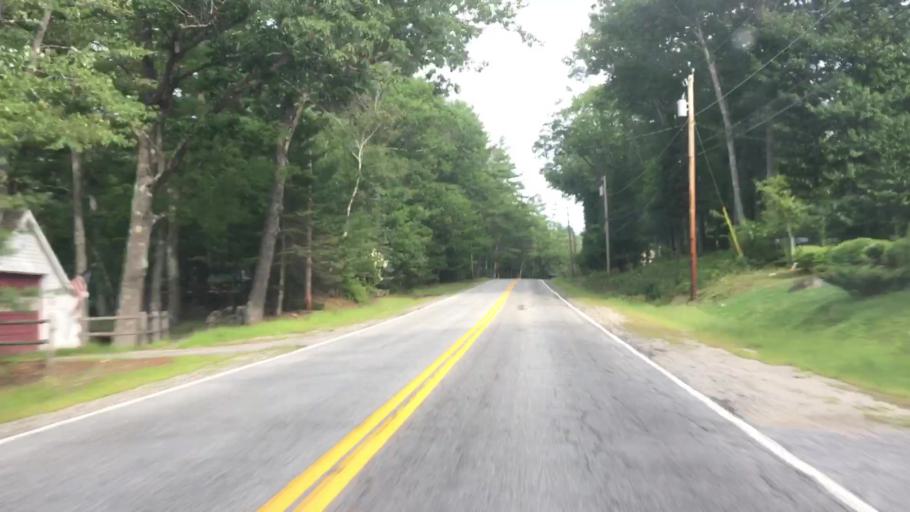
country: US
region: Maine
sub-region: Oxford County
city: Norway
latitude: 44.2215
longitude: -70.6136
